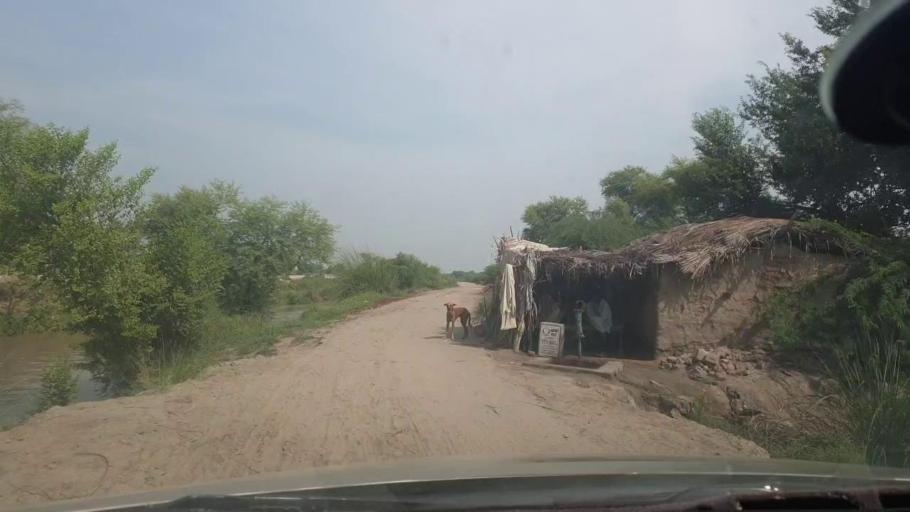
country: PK
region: Sindh
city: Jacobabad
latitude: 28.3110
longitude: 68.4724
